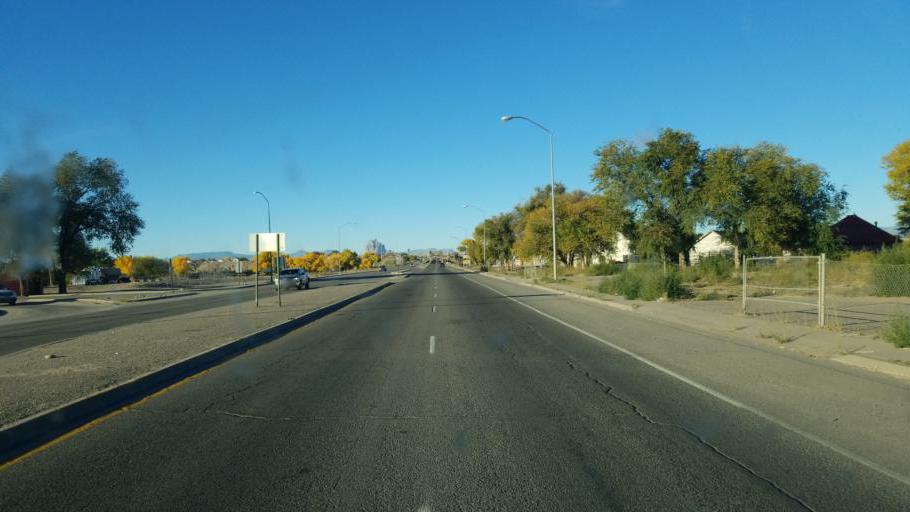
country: US
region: New Mexico
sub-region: San Juan County
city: Shiprock
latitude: 36.7845
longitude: -108.6861
